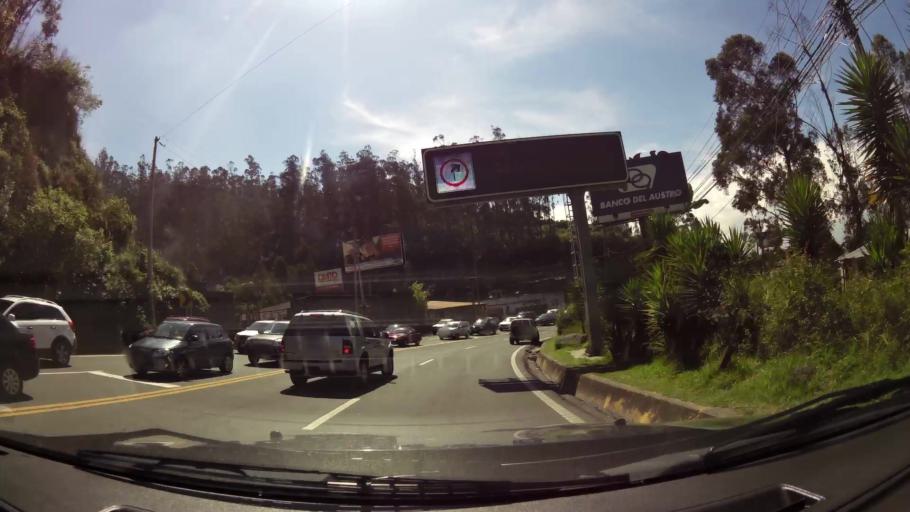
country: EC
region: Pichincha
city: Quito
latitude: -0.1908
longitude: -78.4580
